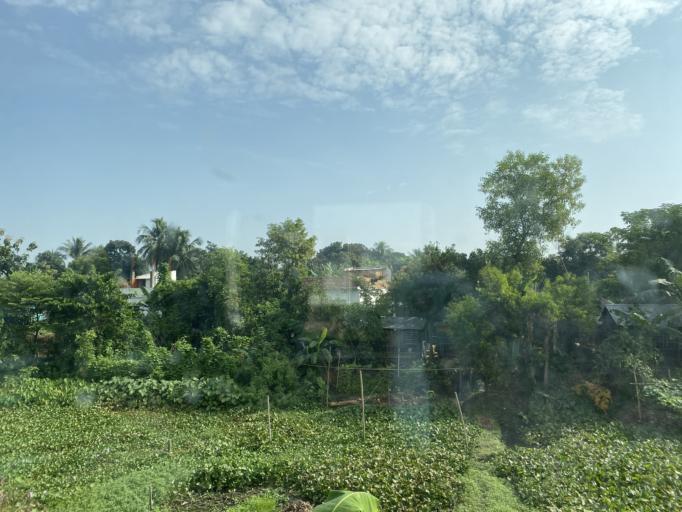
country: BD
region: Dhaka
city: Bhairab Bazar
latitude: 23.9633
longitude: 91.1177
